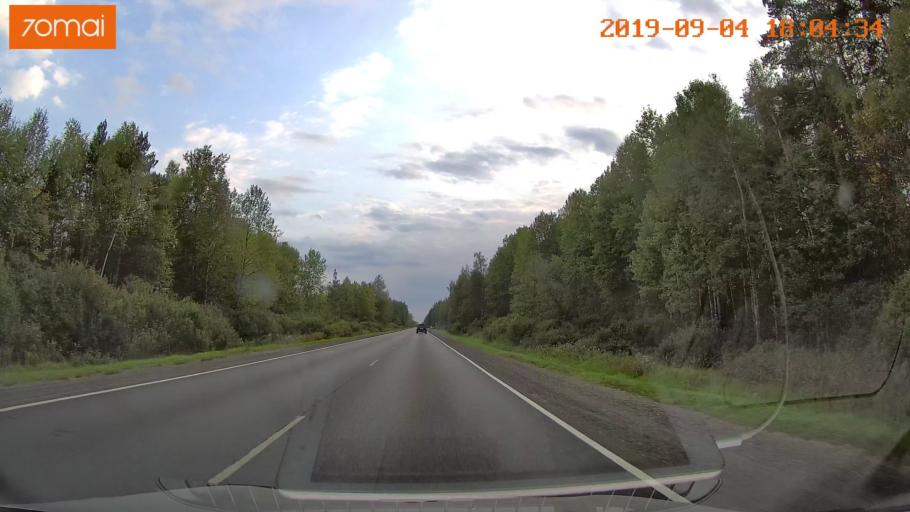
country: RU
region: Moskovskaya
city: Il'inskiy Pogost
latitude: 55.4508
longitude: 38.8375
